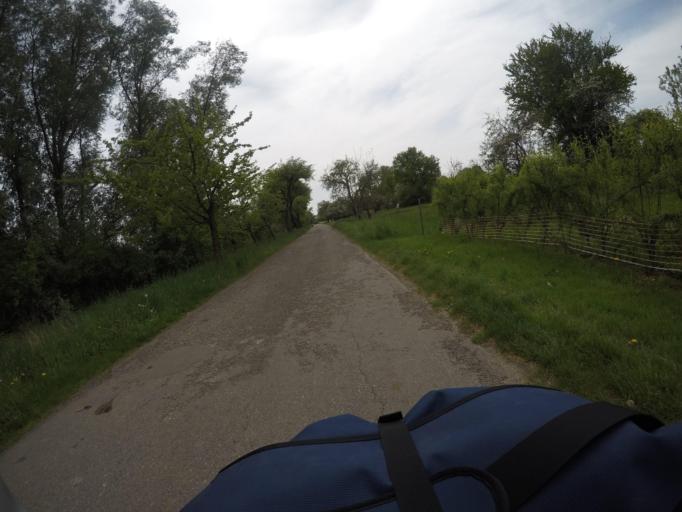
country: DE
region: Baden-Wuerttemberg
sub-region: Freiburg Region
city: Kehl
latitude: 48.5972
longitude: 7.8412
